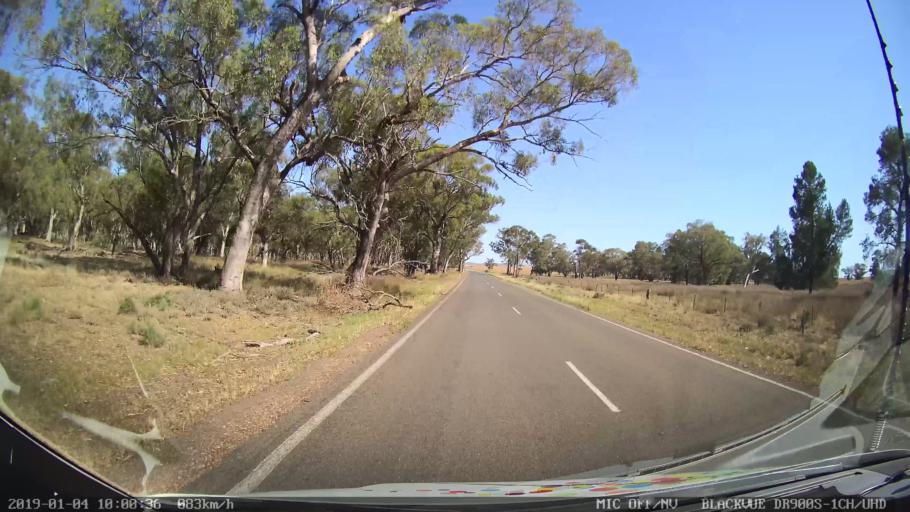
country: AU
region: New South Wales
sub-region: Cabonne
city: Canowindra
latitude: -33.4958
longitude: 148.3779
